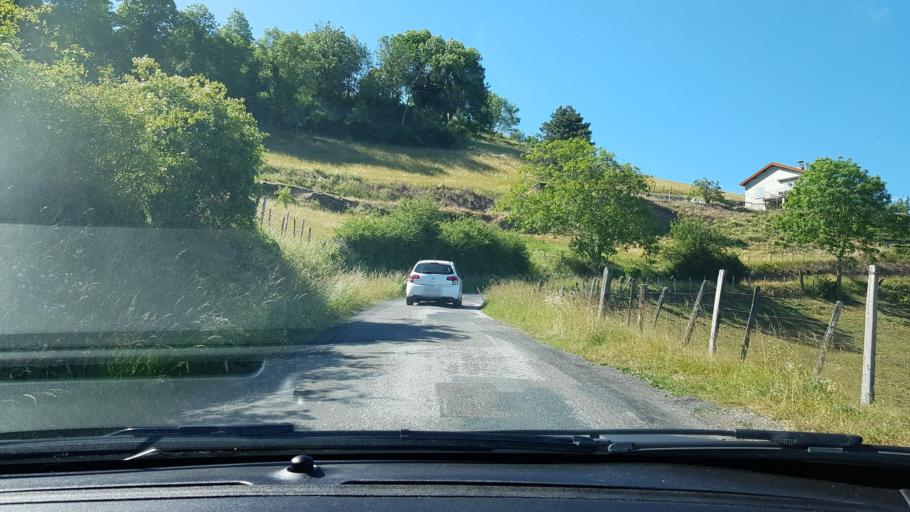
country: FR
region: Rhone-Alpes
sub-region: Departement du Rhone
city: Saint-Didier-sous-Riverie
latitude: 45.5979
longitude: 4.5910
